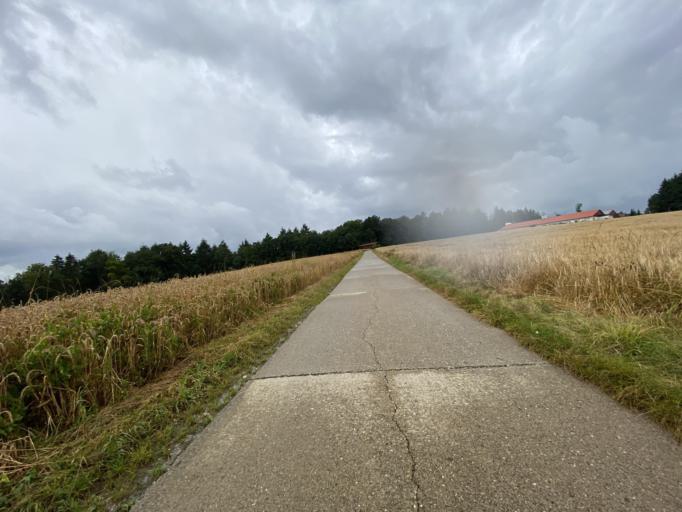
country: DE
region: Baden-Wuerttemberg
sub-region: Tuebingen Region
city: Bingen
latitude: 48.1153
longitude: 9.2568
